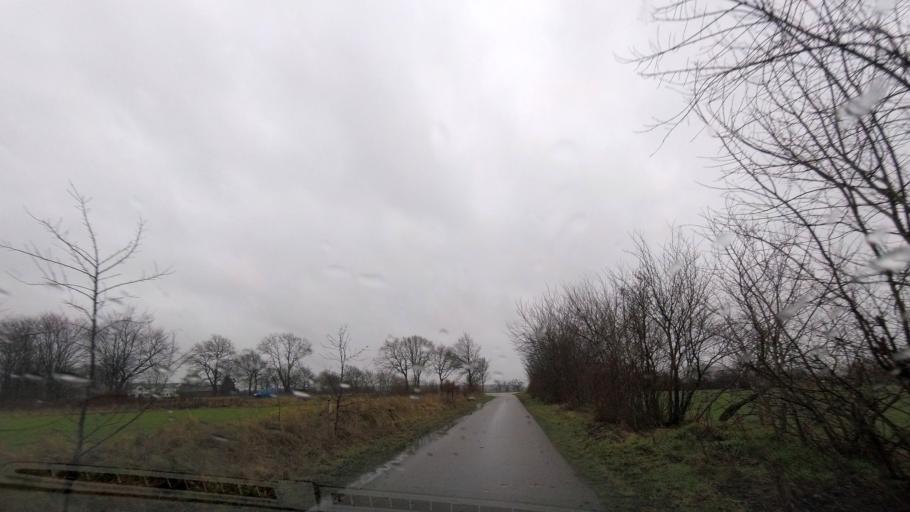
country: DE
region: Schleswig-Holstein
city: Wanderup
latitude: 54.6748
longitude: 9.3094
